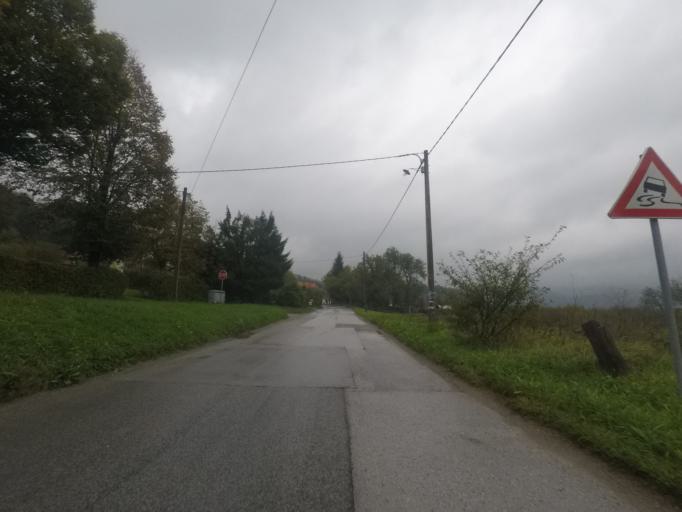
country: HR
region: Karlovacka
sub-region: Grad Ogulin
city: Ogulin
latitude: 45.2910
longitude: 15.1822
